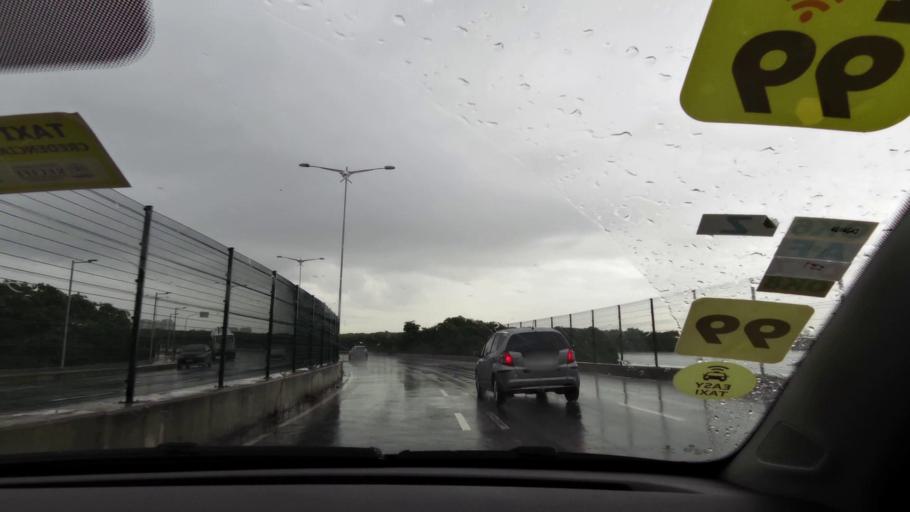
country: BR
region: Pernambuco
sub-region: Recife
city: Recife
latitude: -8.1211
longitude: -34.9015
